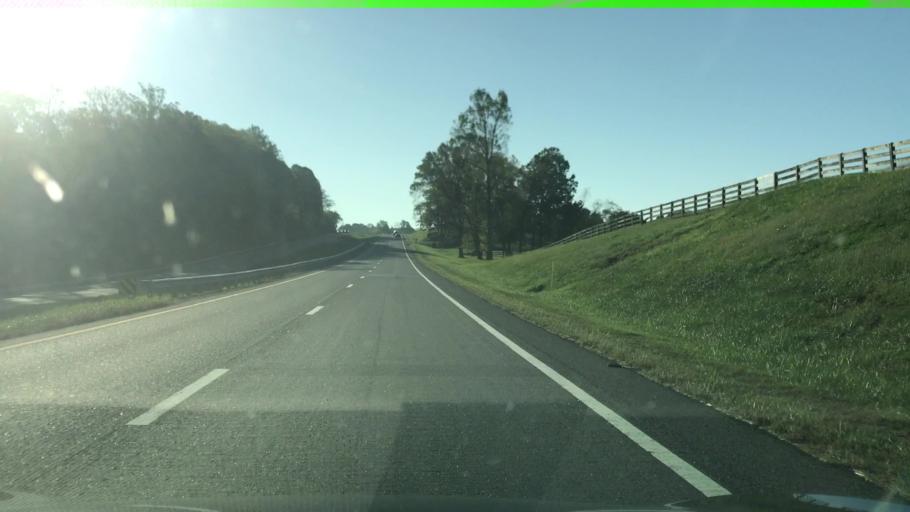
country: US
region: Virginia
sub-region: Bedford County
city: Forest
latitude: 37.3059
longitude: -79.3900
